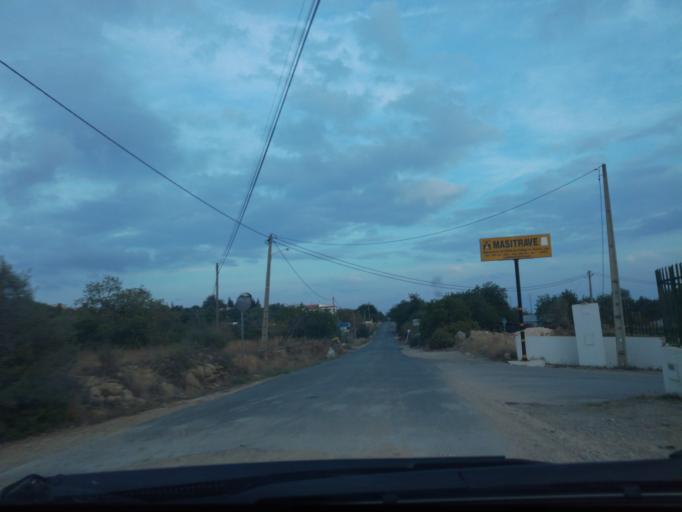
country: PT
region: Faro
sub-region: Olhao
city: Olhao
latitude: 37.0838
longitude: -7.8704
